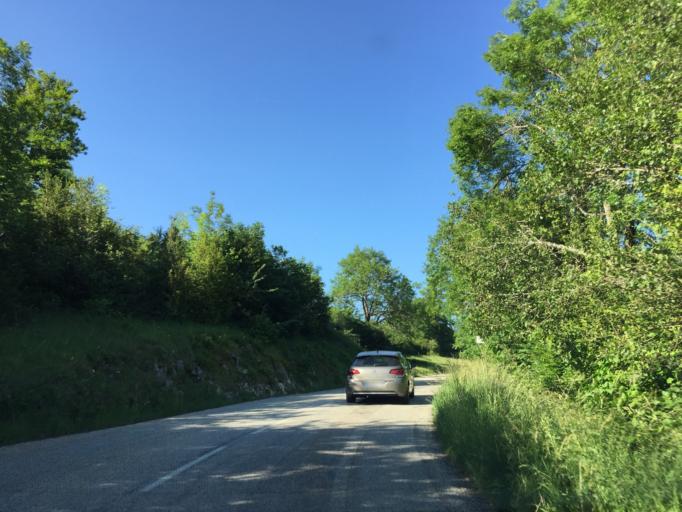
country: FR
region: Rhone-Alpes
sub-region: Departement de la Drome
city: Saint-Laurent-en-Royans
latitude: 44.9498
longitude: 5.3980
